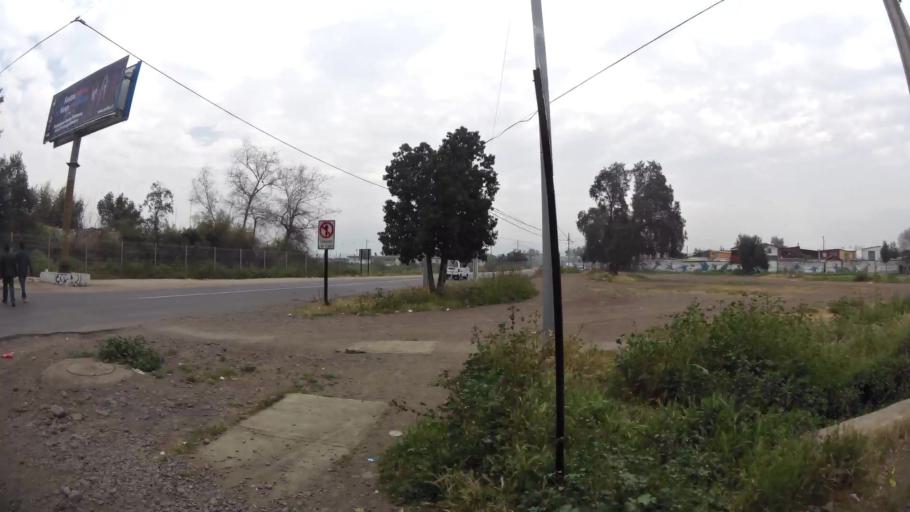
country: CL
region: Santiago Metropolitan
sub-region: Provincia de Chacabuco
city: Chicureo Abajo
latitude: -33.2096
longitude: -70.6849
